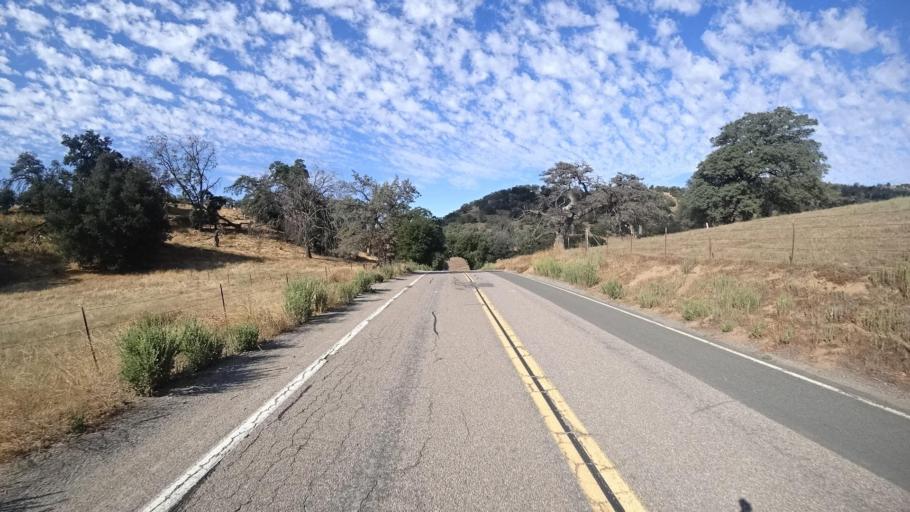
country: US
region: California
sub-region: San Diego County
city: Julian
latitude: 33.2065
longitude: -116.7499
